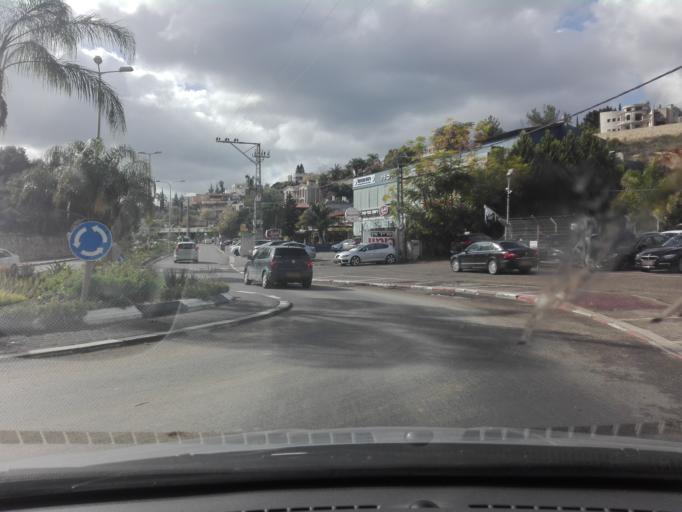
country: IL
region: Haifa
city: Daliyat el Karmil
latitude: 32.7016
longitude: 35.0577
